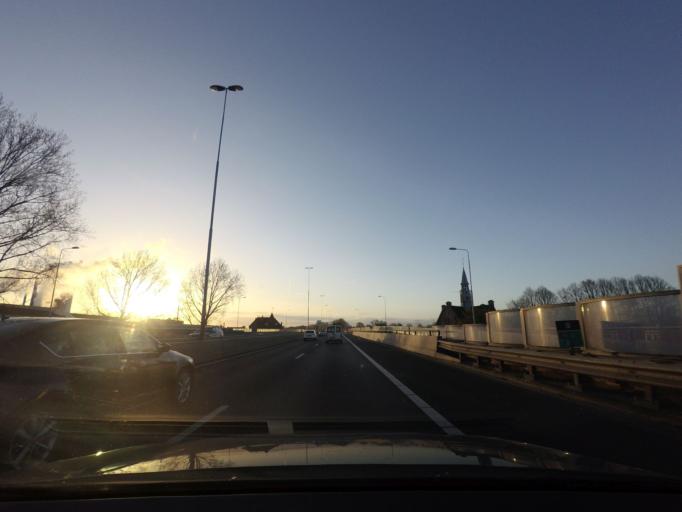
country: NL
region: North Holland
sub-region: Gemeente Zaanstad
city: Zaanstad
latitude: 52.4638
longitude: 4.8089
